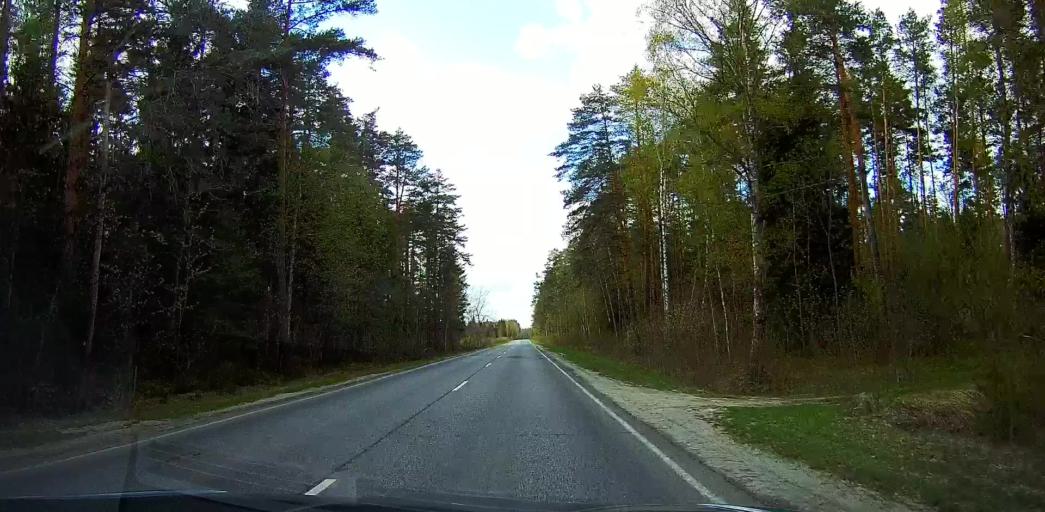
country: RU
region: Moskovskaya
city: Rakhmanovo
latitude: 55.6472
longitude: 38.6719
